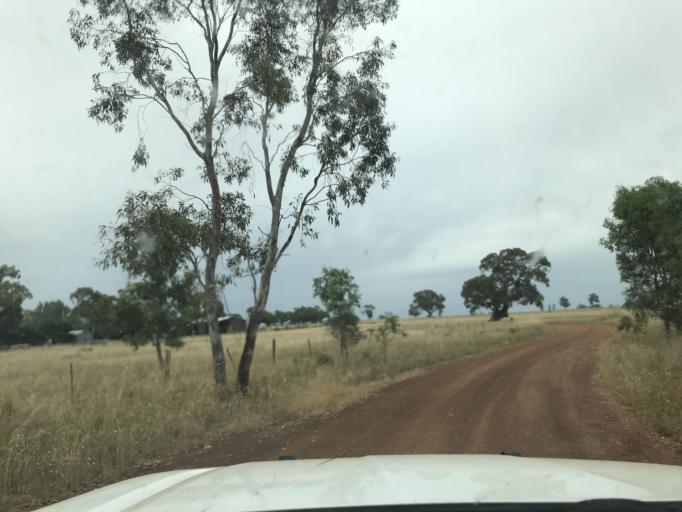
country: AU
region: Victoria
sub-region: Horsham
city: Horsham
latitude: -37.0717
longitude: 141.6648
